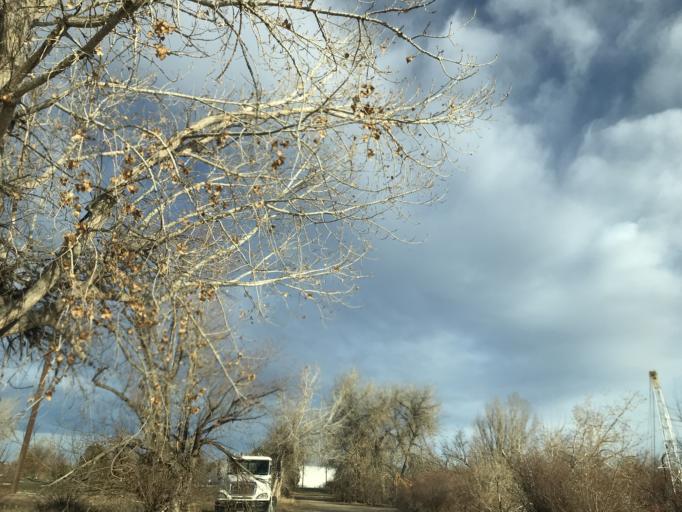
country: US
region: Colorado
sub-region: Arapahoe County
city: Littleton
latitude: 39.6106
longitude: -105.0259
